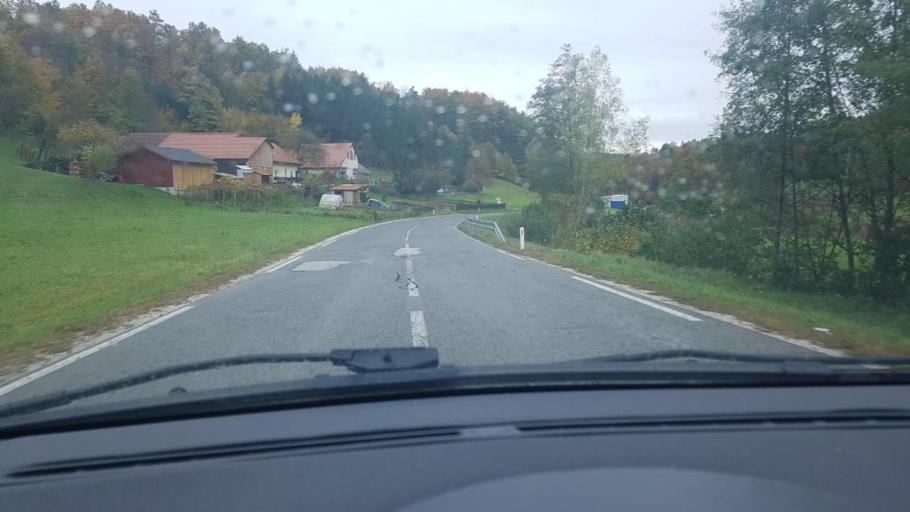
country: SI
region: Rogatec
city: Rogatec
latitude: 46.2508
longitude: 15.7011
